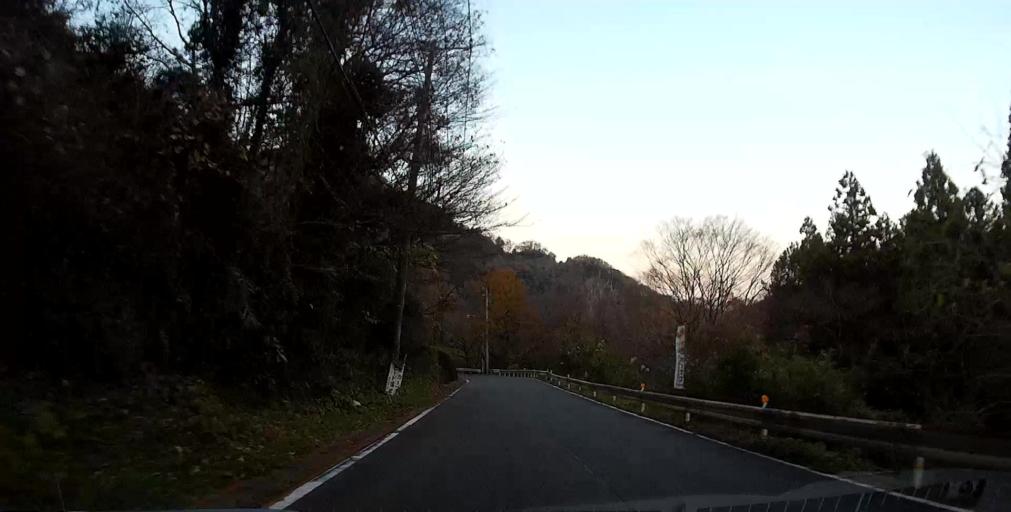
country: JP
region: Yamanashi
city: Uenohara
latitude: 35.5652
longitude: 139.2082
